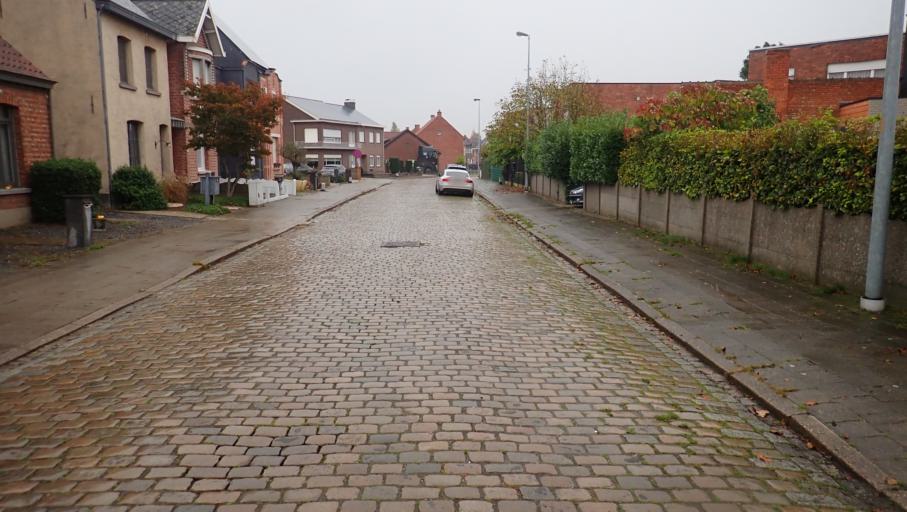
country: BE
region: Flanders
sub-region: Provincie Antwerpen
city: Berlaar
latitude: 51.1139
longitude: 4.6511
